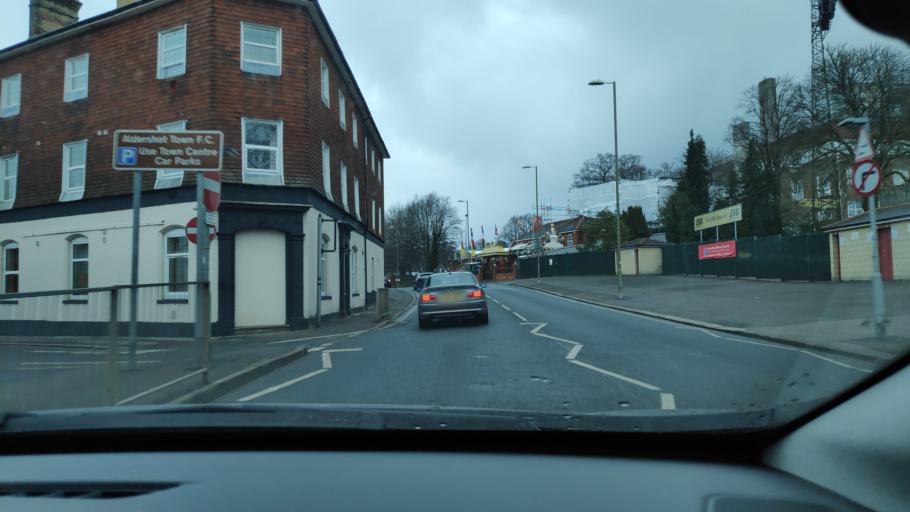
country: GB
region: England
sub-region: Hampshire
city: Aldershot
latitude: 51.2478
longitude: -0.7561
